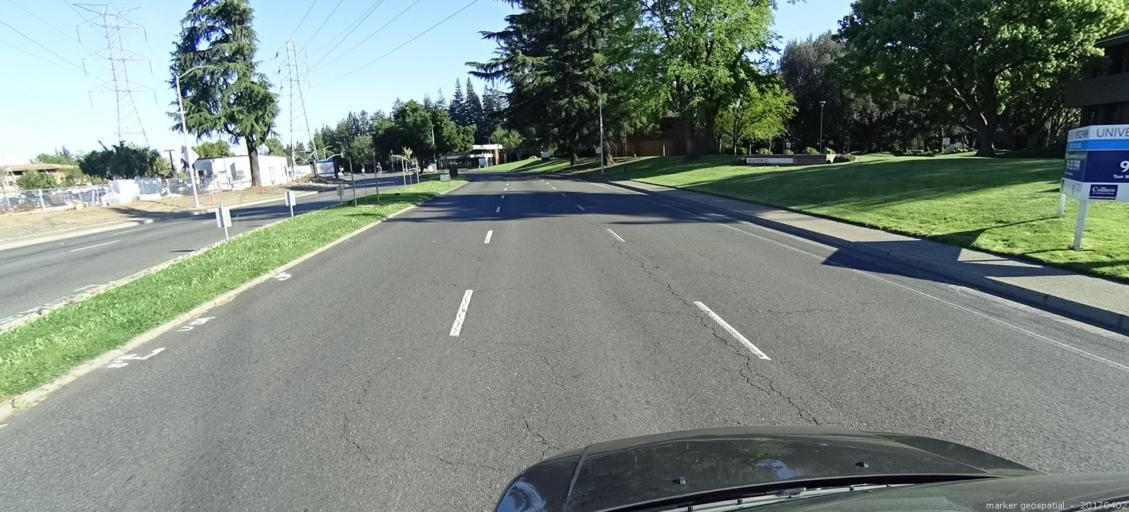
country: US
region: California
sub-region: Sacramento County
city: Arden-Arcade
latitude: 38.5732
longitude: -121.4150
